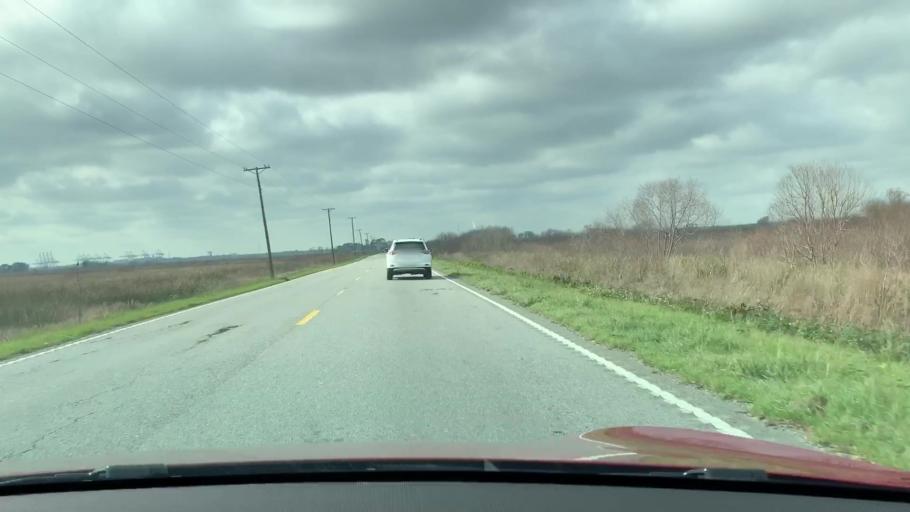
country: US
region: Georgia
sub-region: Chatham County
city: Port Wentworth
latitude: 32.1722
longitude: -81.0995
